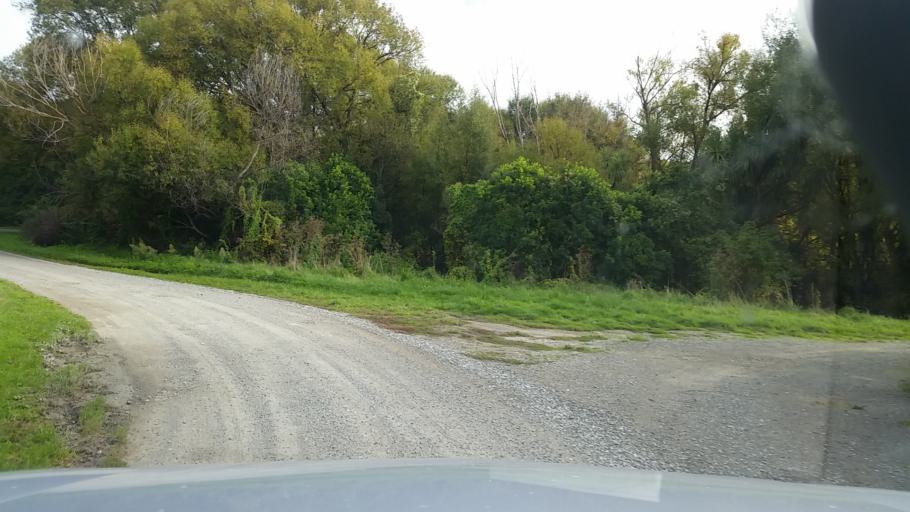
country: NZ
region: Marlborough
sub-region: Marlborough District
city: Blenheim
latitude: -41.4769
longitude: 173.9851
